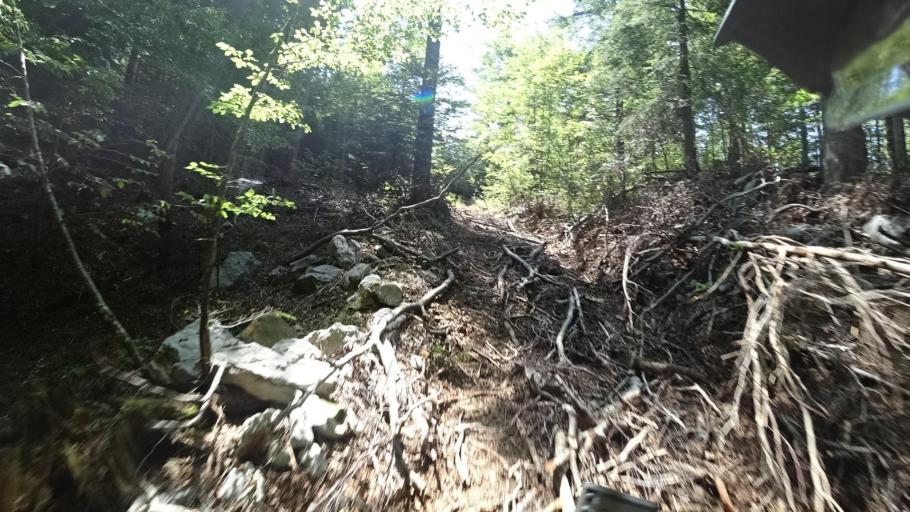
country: HR
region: Primorsko-Goranska
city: Bribir
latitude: 45.2692
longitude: 14.8402
